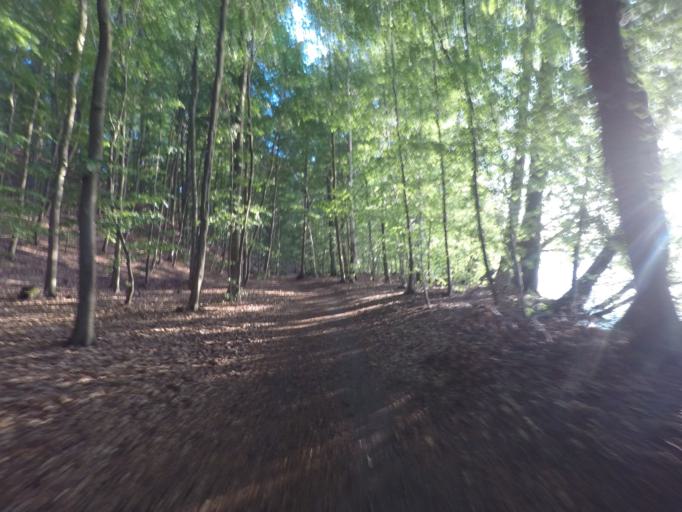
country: DE
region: Brandenburg
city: Joachimsthal
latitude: 52.9071
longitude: 13.6949
